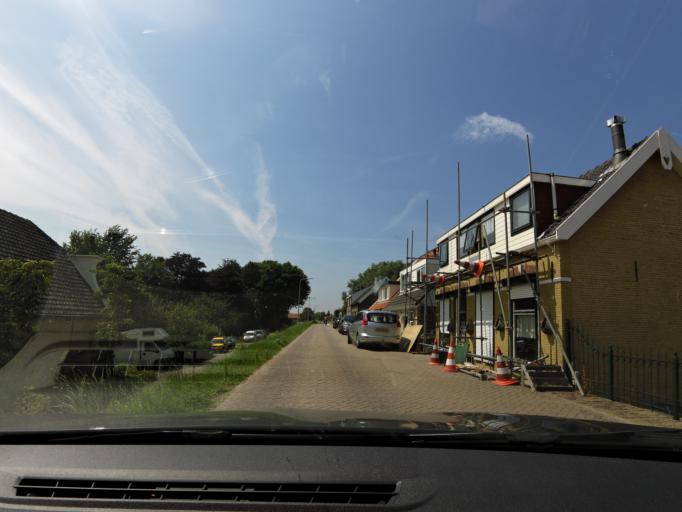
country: NL
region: South Holland
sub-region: Gemeente Binnenmaas
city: Heinenoord
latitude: 51.8265
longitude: 4.4701
